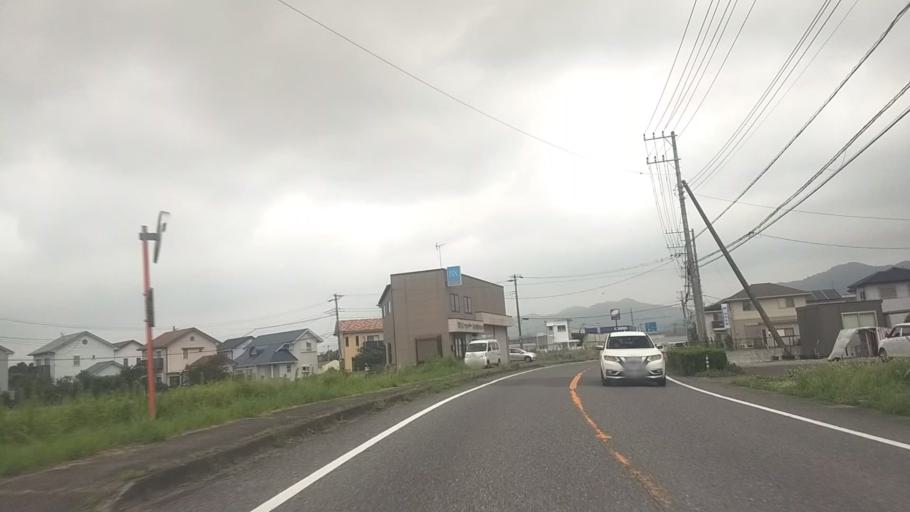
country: JP
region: Chiba
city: Kawaguchi
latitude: 35.1194
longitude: 140.0713
